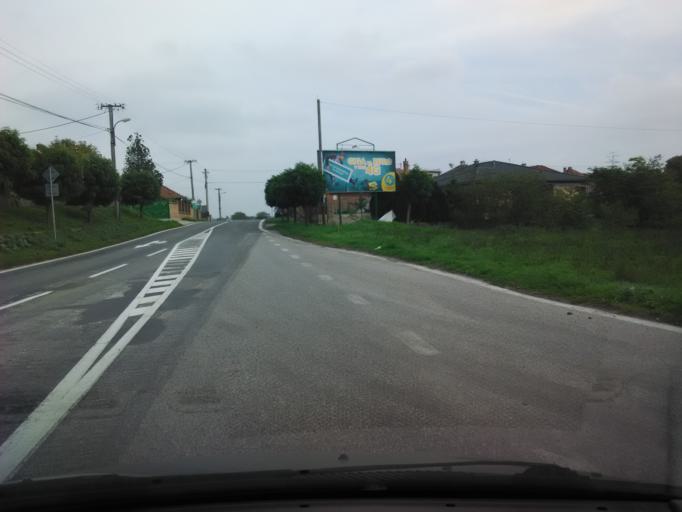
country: SK
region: Nitriansky
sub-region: Okres Nove Zamky
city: Nove Zamky
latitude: 47.9941
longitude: 18.2752
